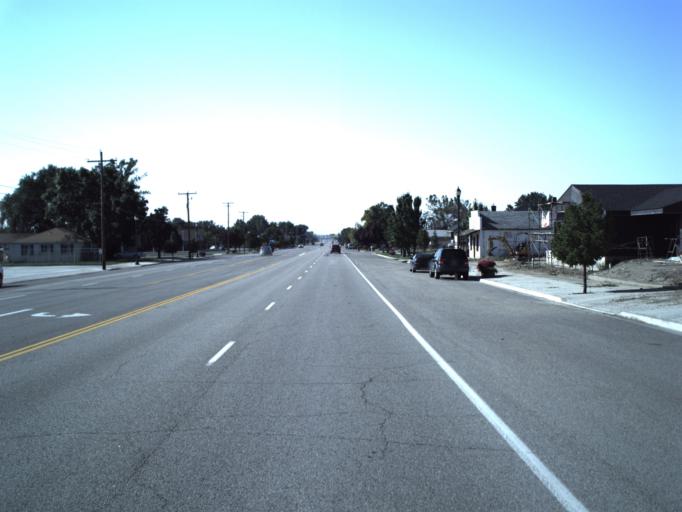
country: US
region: Utah
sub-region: Emery County
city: Huntington
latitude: 39.3334
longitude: -110.9648
